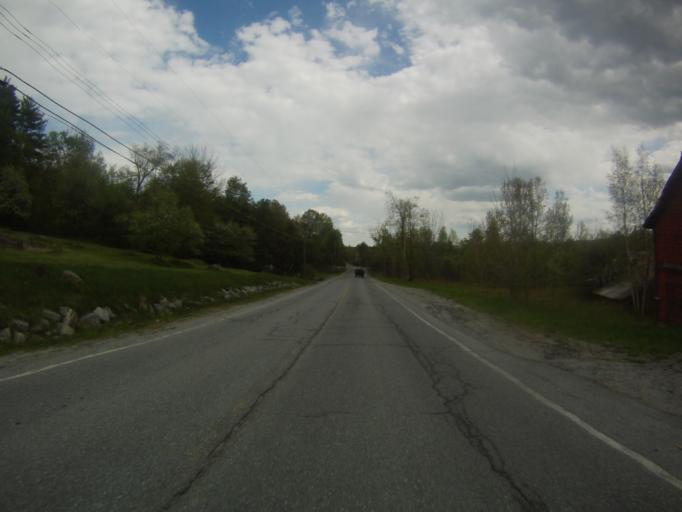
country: US
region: New York
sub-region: Essex County
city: Mineville
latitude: 44.0750
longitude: -73.5265
